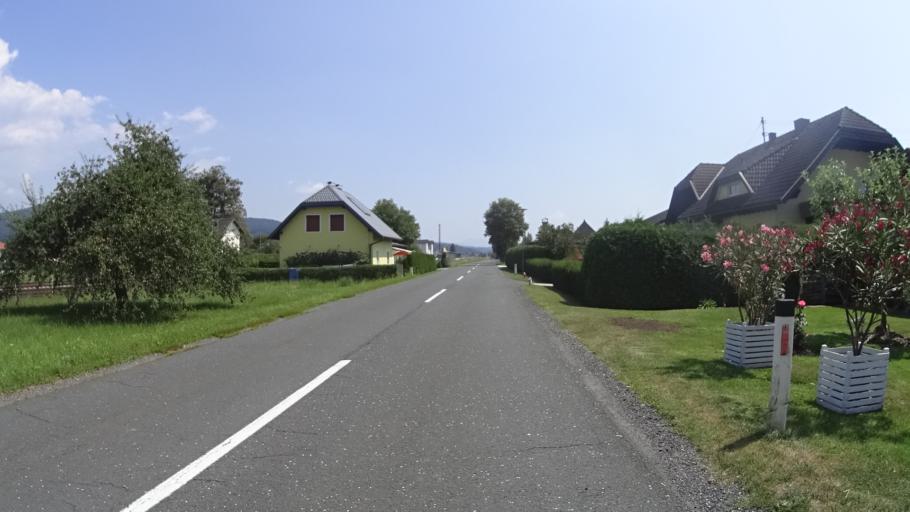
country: AT
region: Carinthia
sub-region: Politischer Bezirk Volkermarkt
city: Bleiburg/Pliberk
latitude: 46.5748
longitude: 14.7813
